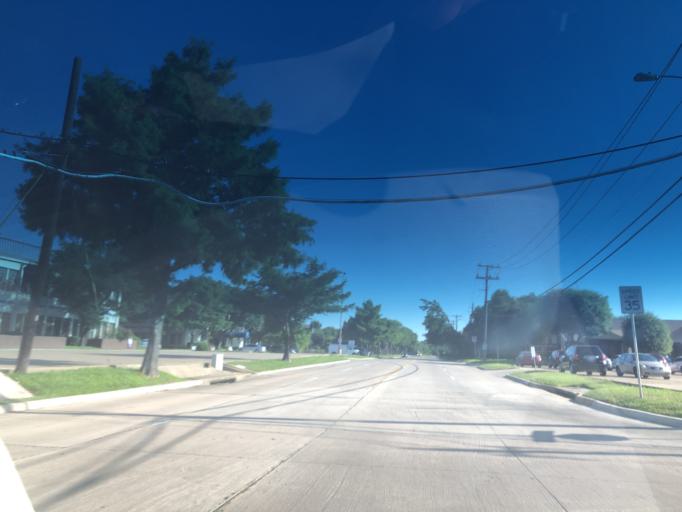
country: US
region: Texas
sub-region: Dallas County
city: Grand Prairie
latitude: 32.7103
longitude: -97.0024
